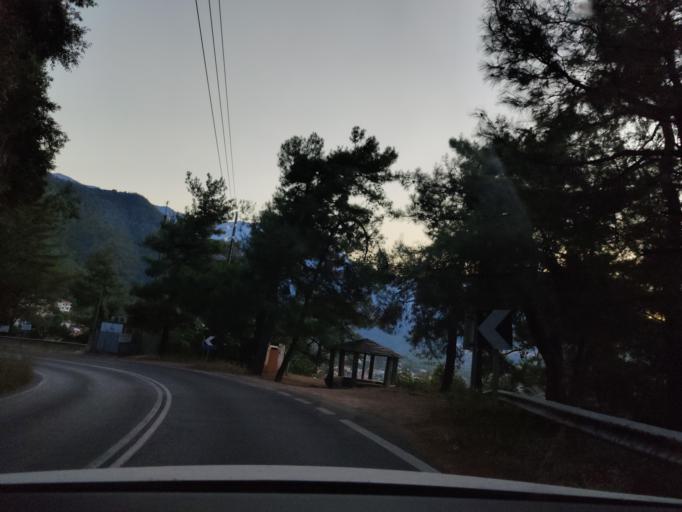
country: GR
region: East Macedonia and Thrace
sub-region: Nomos Kavalas
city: Potamia
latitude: 40.7082
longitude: 24.7641
